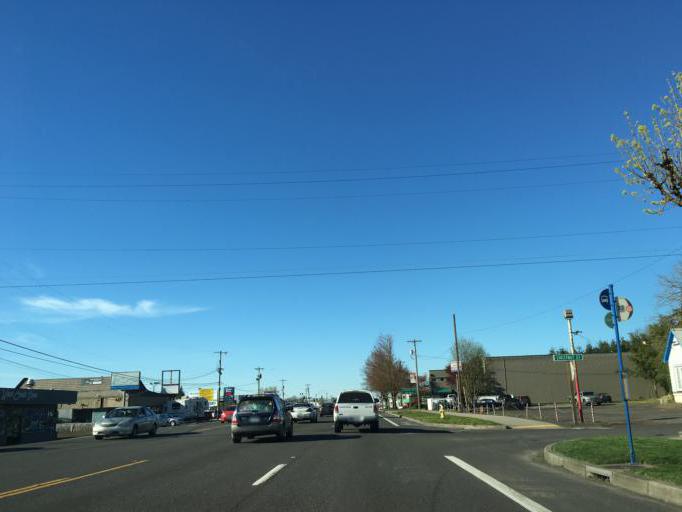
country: US
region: Oregon
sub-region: Clackamas County
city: Oak Grove
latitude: 45.4196
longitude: -122.6329
